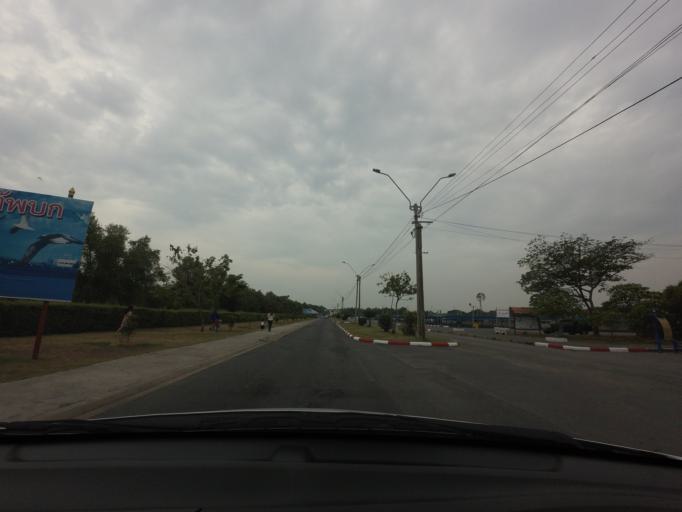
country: TH
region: Samut Prakan
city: Samut Prakan
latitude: 13.5197
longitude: 100.6555
